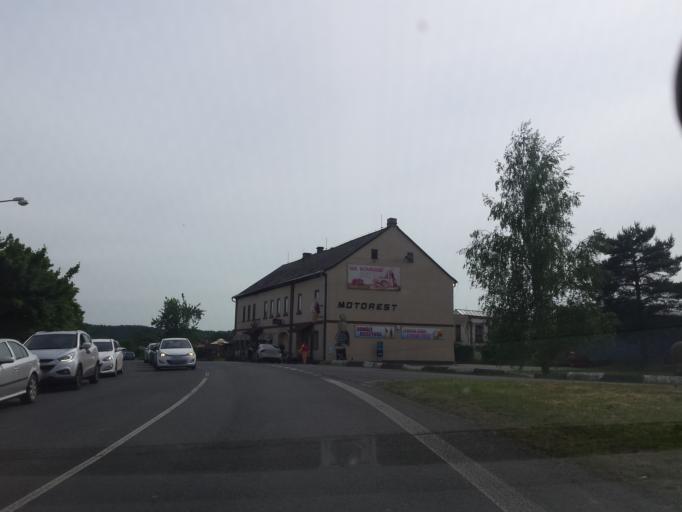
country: CZ
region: Liberecky
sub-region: Okres Ceska Lipa
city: Ceska Lipa
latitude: 50.6284
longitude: 14.5354
